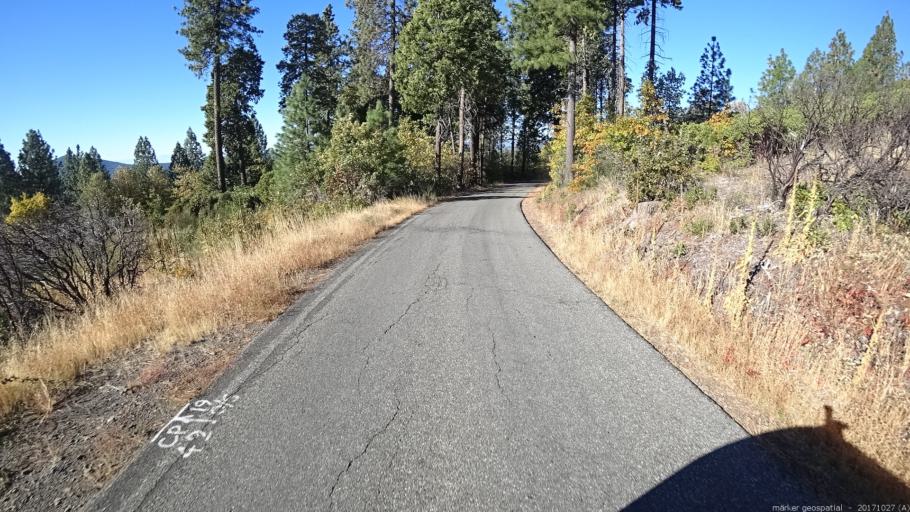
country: US
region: California
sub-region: Shasta County
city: Burney
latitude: 40.8597
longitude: -121.9165
